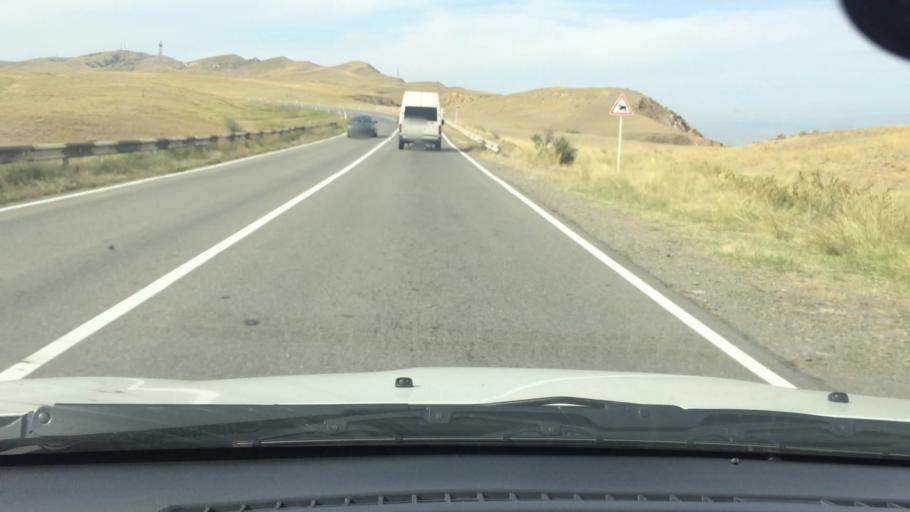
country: GE
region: Kvemo Kartli
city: Rust'avi
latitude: 41.5316
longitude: 44.9775
